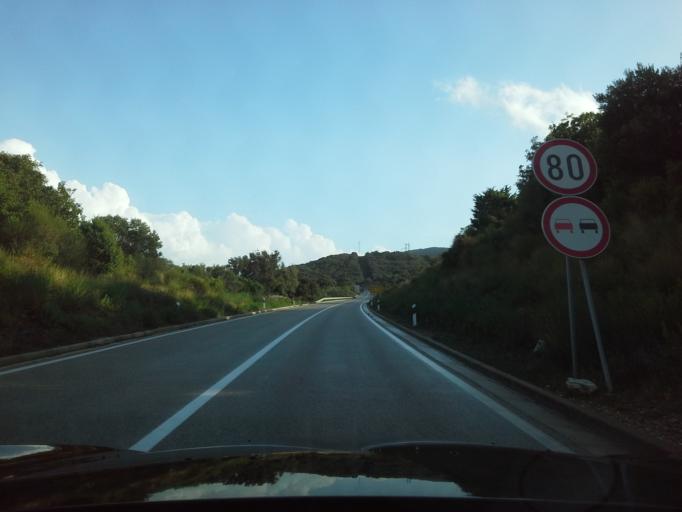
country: HR
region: Primorsko-Goranska
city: Mali Losinj
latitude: 44.6586
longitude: 14.3899
